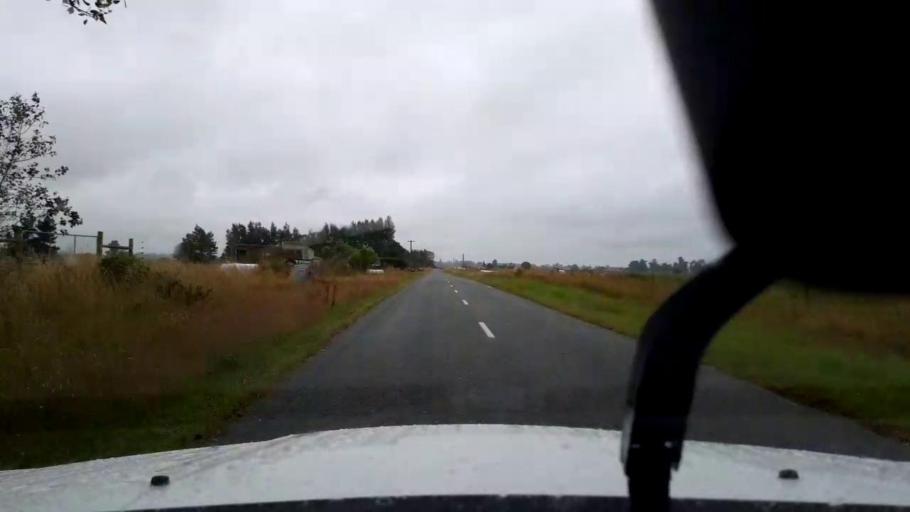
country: NZ
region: Canterbury
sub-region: Timaru District
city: Pleasant Point
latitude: -44.2515
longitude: 171.2268
